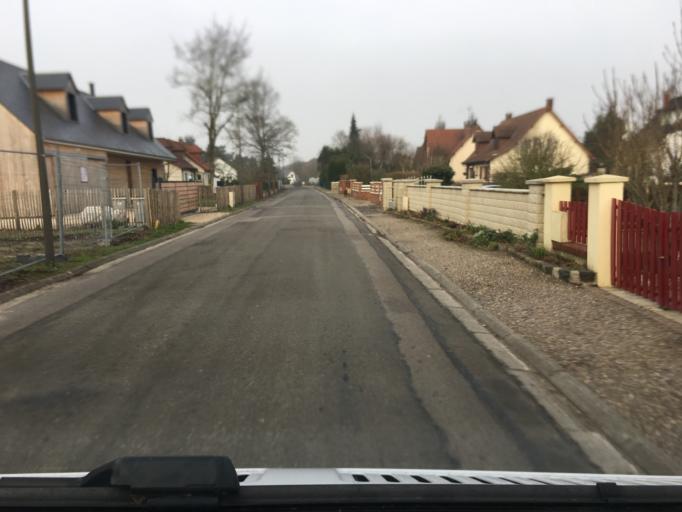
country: FR
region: Picardie
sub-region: Departement de la Somme
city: Saint-Valery-sur-Somme
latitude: 50.1812
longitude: 1.6311
